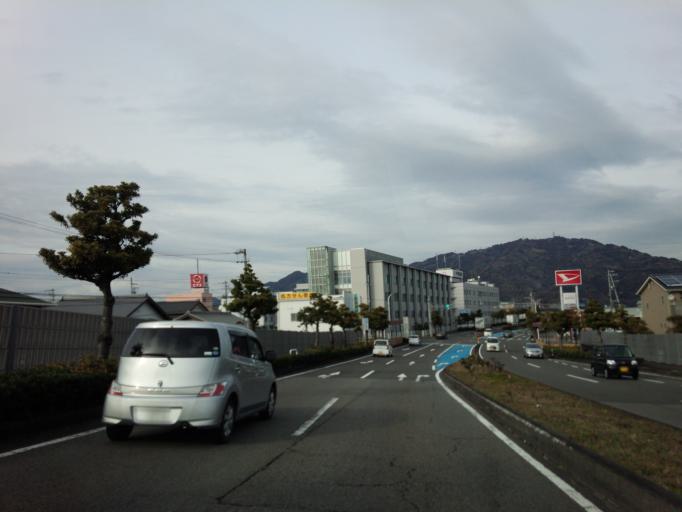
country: JP
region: Shizuoka
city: Yaizu
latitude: 34.8738
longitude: 138.2993
